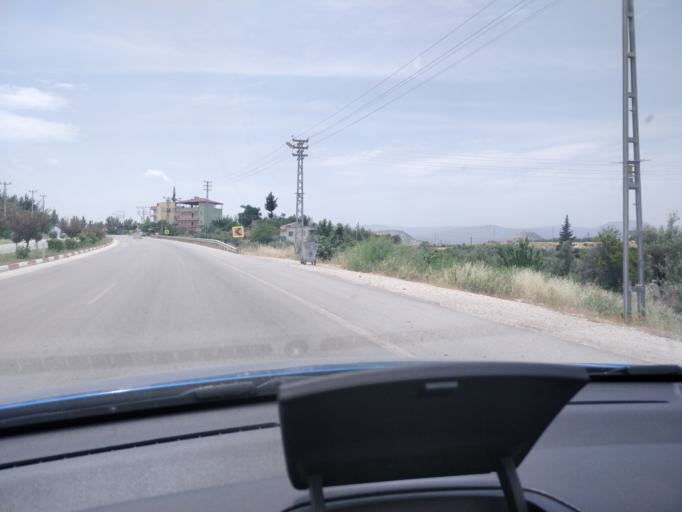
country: TR
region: Mersin
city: Mut
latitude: 36.6194
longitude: 33.4418
